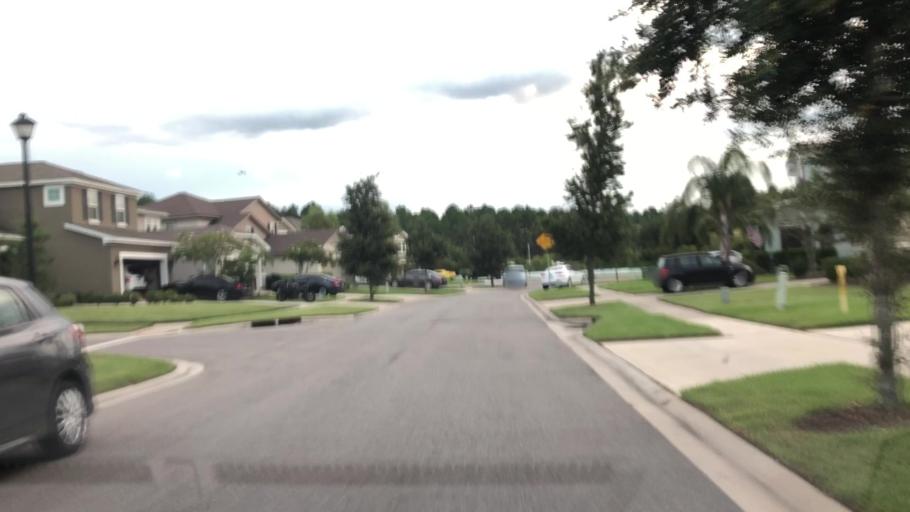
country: US
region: Florida
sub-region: Saint Johns County
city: Palm Valley
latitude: 30.0972
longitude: -81.4648
